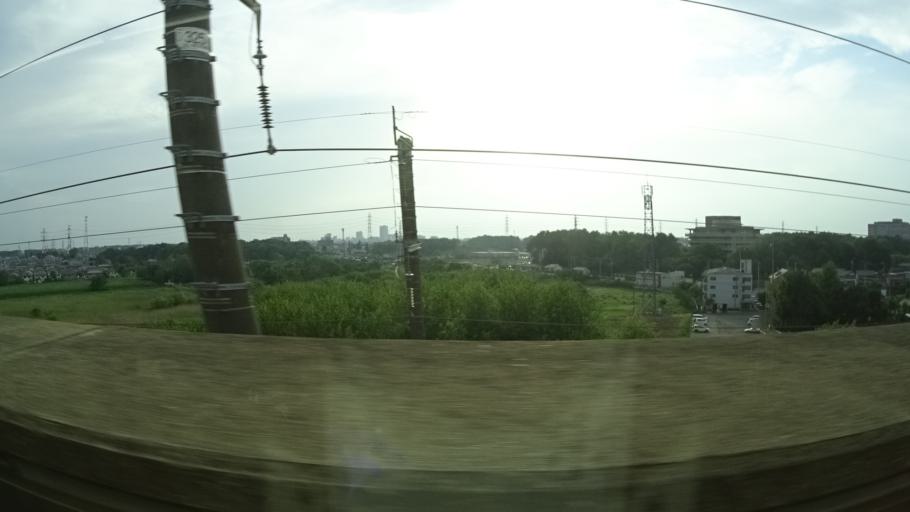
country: JP
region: Saitama
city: Ageoshimo
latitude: 35.9791
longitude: 139.6248
